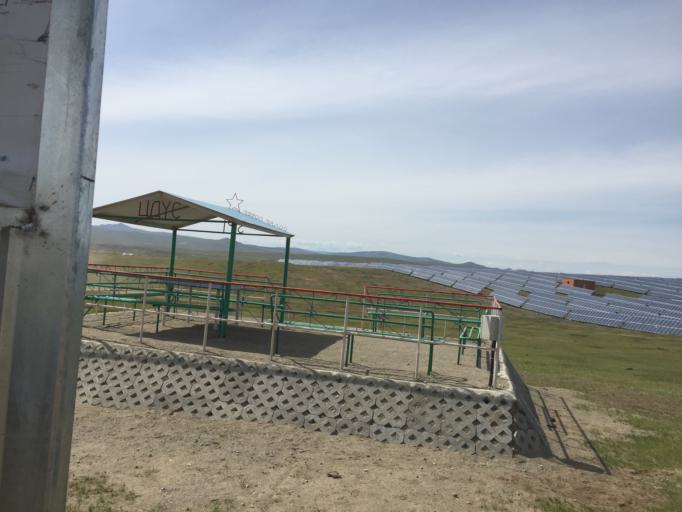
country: MN
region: Darhan Uul
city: Darhan
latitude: 49.3970
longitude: 105.9449
